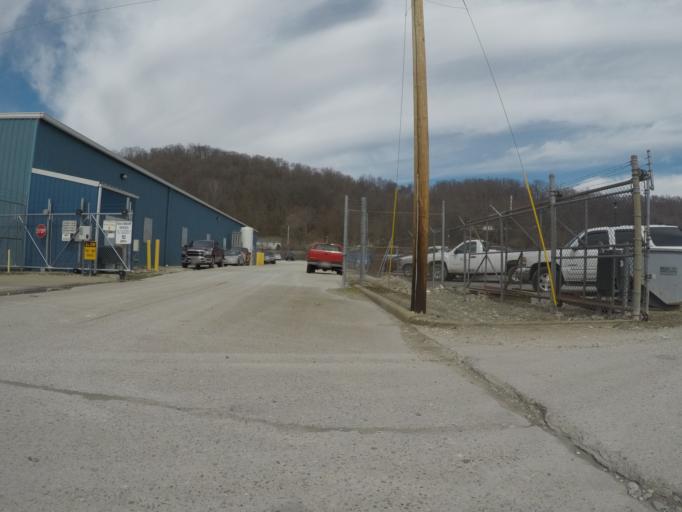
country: US
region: West Virginia
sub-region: Cabell County
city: Pea Ridge
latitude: 38.4158
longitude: -82.3692
